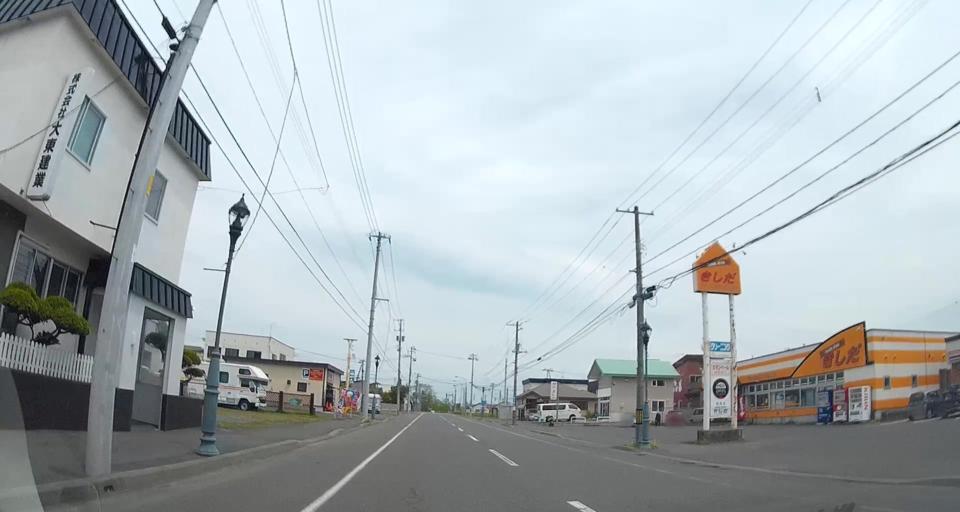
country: JP
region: Hokkaido
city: Chitose
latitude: 42.7669
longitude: 141.8193
